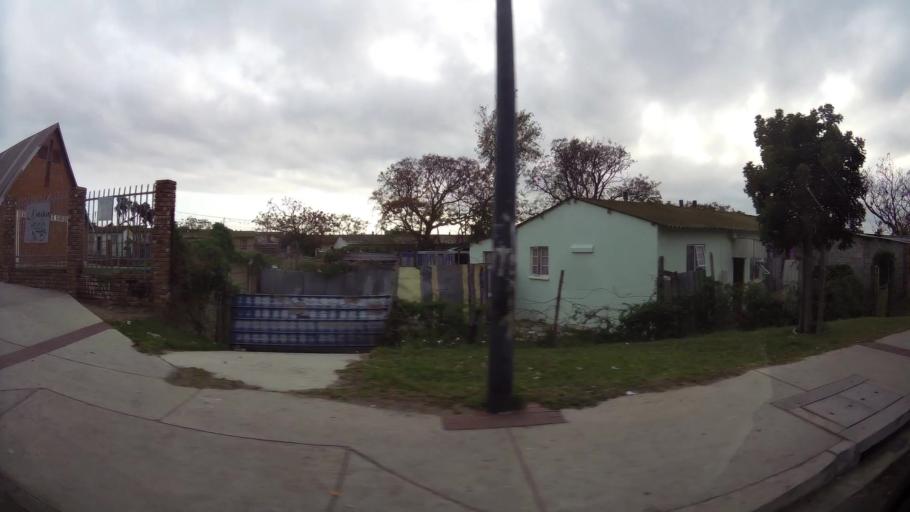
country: ZA
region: Eastern Cape
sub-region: Nelson Mandela Bay Metropolitan Municipality
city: Port Elizabeth
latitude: -33.9086
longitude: 25.5504
